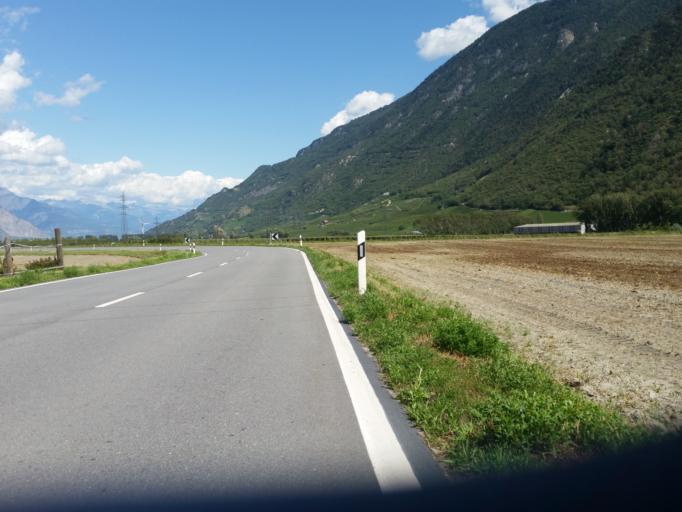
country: CH
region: Valais
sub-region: Martigny District
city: Martigny-Ville
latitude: 46.1070
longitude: 7.1019
